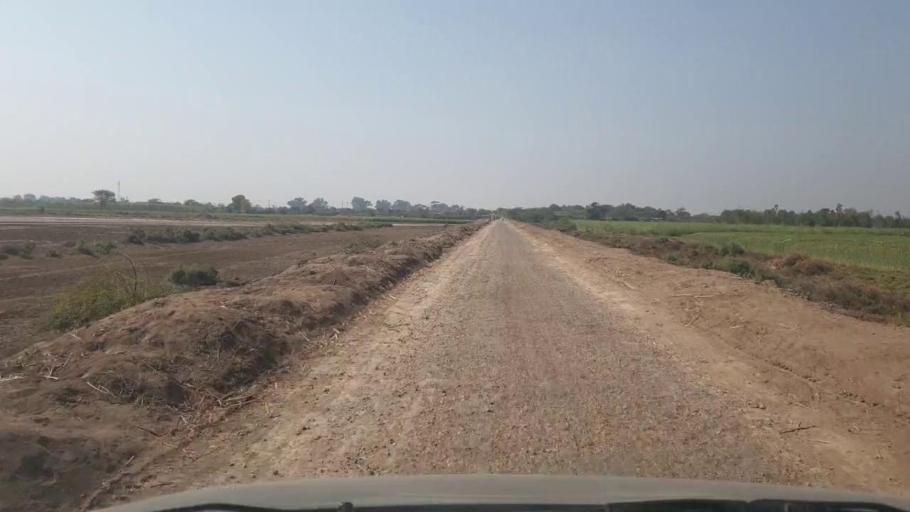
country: PK
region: Sindh
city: Mirwah Gorchani
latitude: 25.2369
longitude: 69.0926
